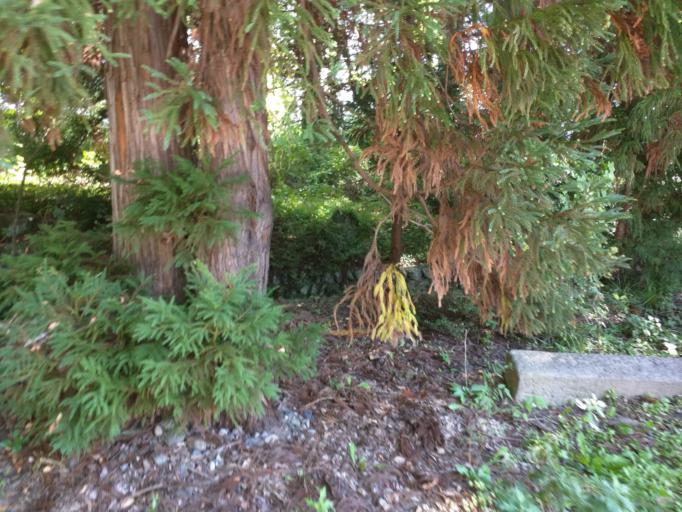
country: JP
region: Fukushima
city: Kitakata
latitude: 37.4554
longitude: 139.8408
